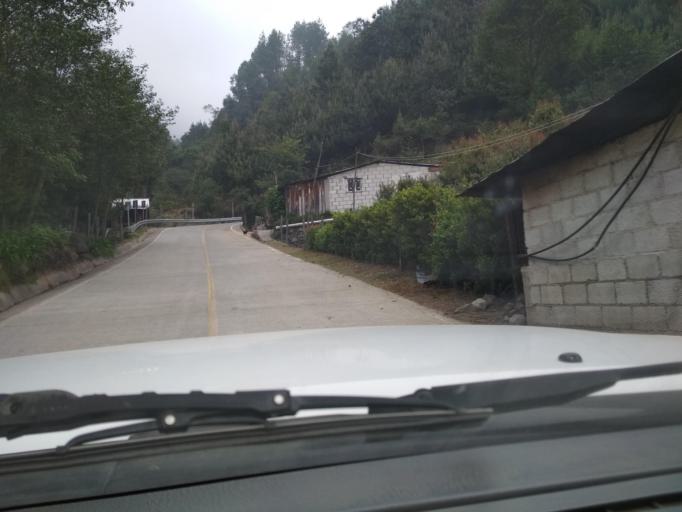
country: MX
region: Veracruz
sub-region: La Perla
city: Chilapa
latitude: 18.9908
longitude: -97.1830
